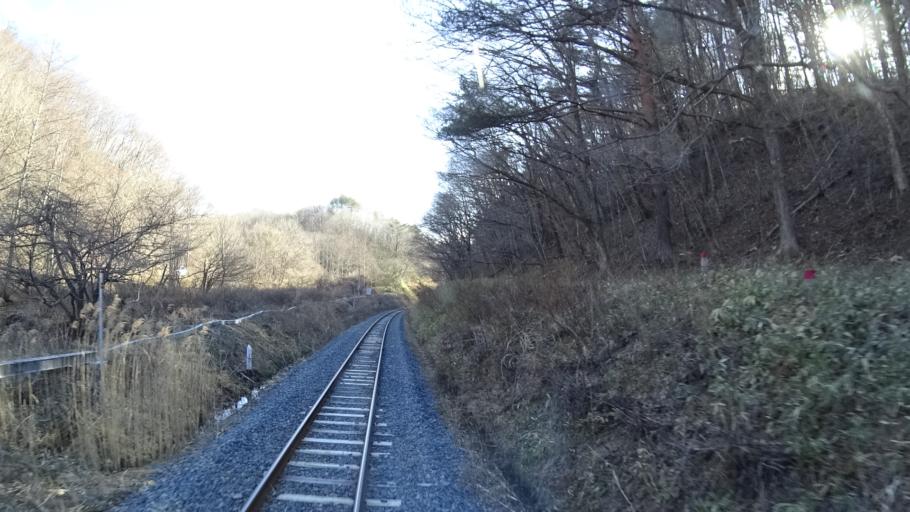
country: JP
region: Iwate
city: Yamada
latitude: 39.4952
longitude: 141.9282
